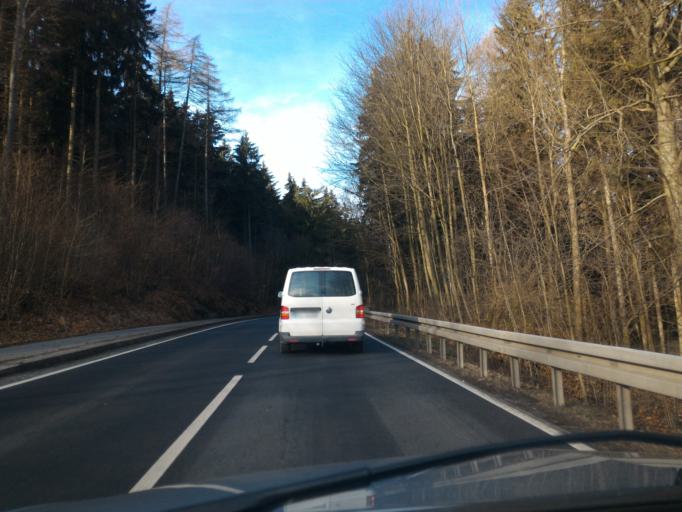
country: DE
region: Saxony
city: Steinigtwolmsdorf
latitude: 51.0566
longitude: 14.3681
